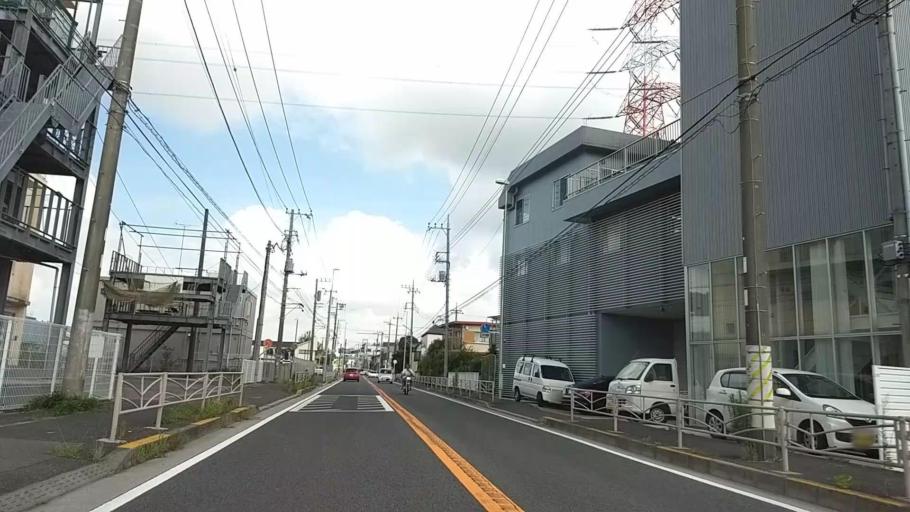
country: JP
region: Kanagawa
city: Minami-rinkan
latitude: 35.4888
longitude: 139.5175
